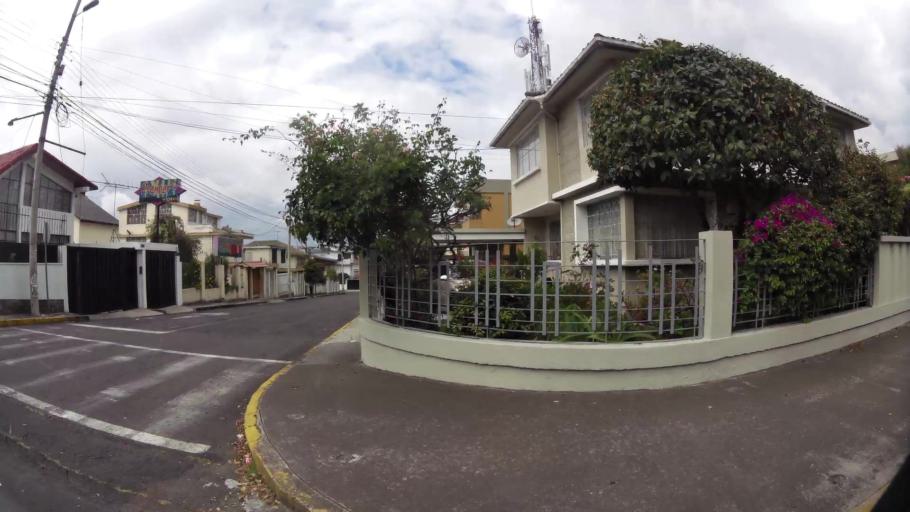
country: EC
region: Pichincha
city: Quito
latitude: -0.1542
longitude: -78.4920
